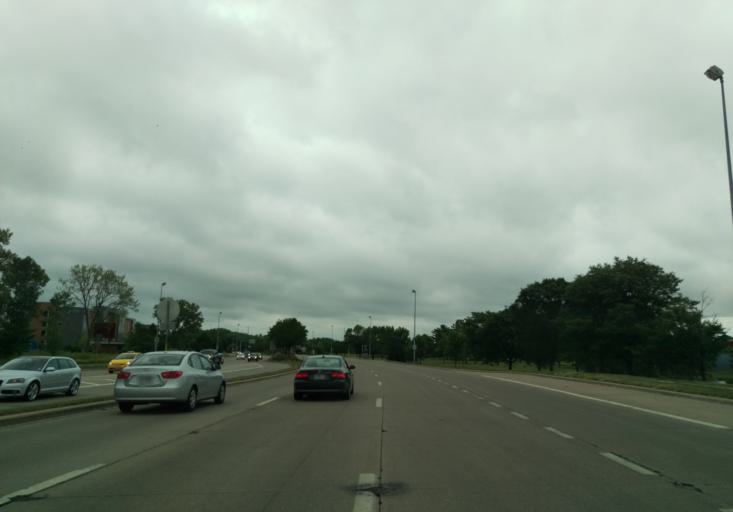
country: US
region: Wisconsin
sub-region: Dane County
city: Madison
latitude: 43.0507
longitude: -89.3779
